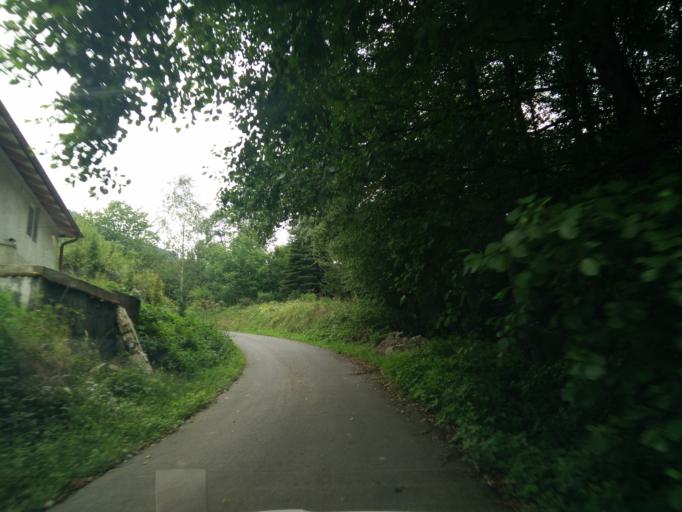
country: SK
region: Banskobystricky
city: Ziar nad Hronom
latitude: 48.5735
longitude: 18.9057
